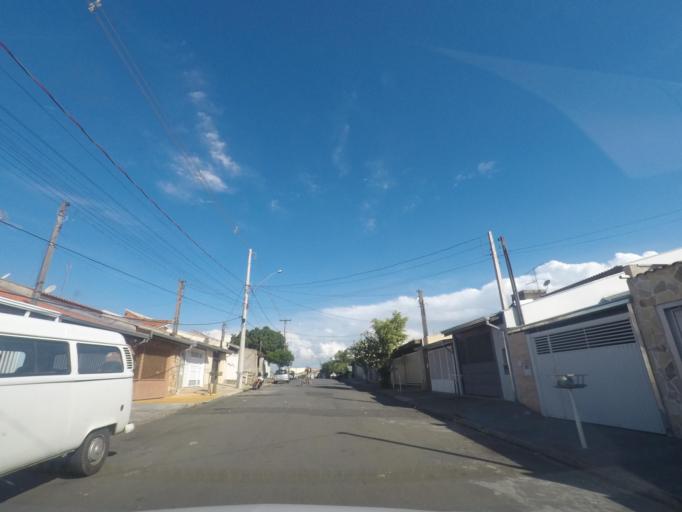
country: BR
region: Sao Paulo
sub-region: Sumare
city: Sumare
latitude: -22.8102
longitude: -47.2660
